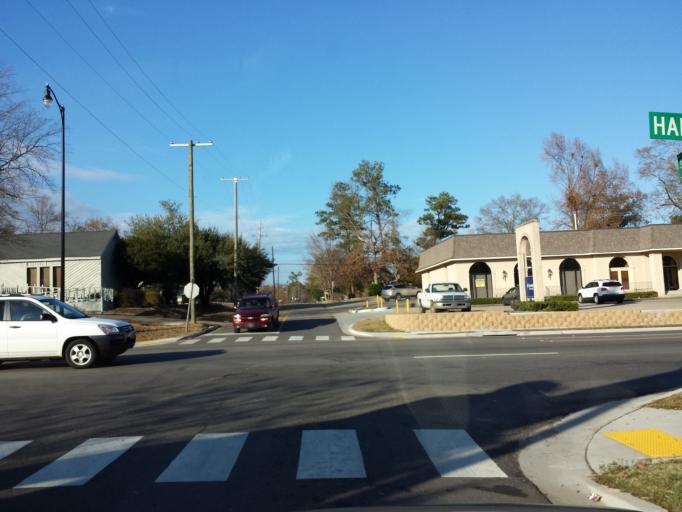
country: US
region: Mississippi
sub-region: Forrest County
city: Hattiesburg
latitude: 31.3246
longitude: -89.3239
